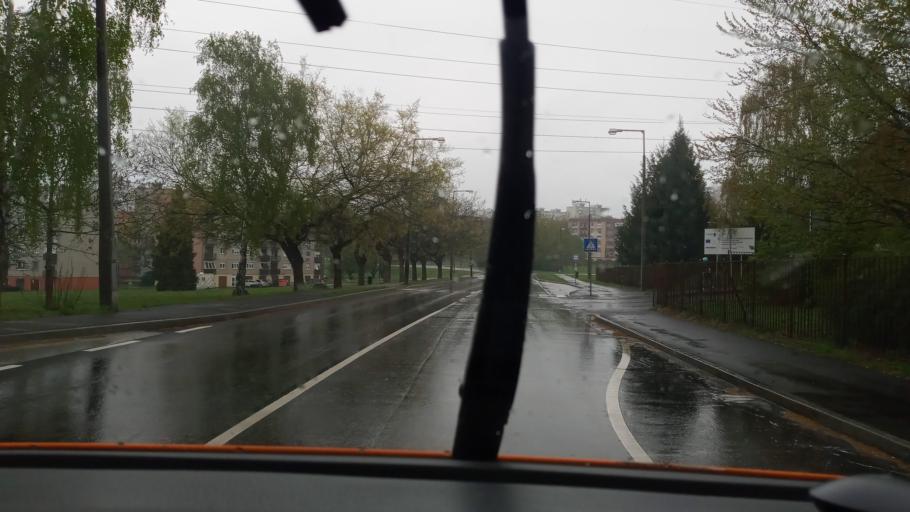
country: HU
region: Baranya
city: Pecs
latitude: 46.0361
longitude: 18.2168
